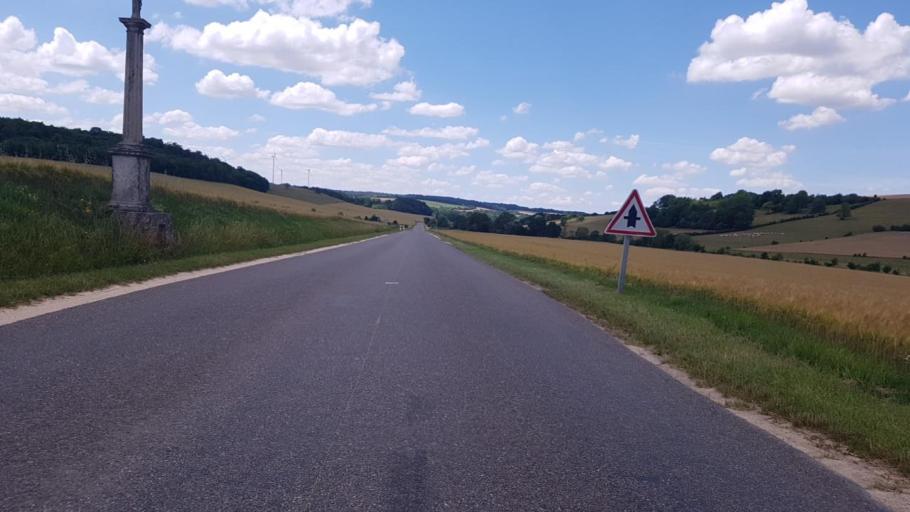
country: FR
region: Lorraine
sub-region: Departement de la Meuse
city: Vacon
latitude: 48.6388
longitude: 5.5059
